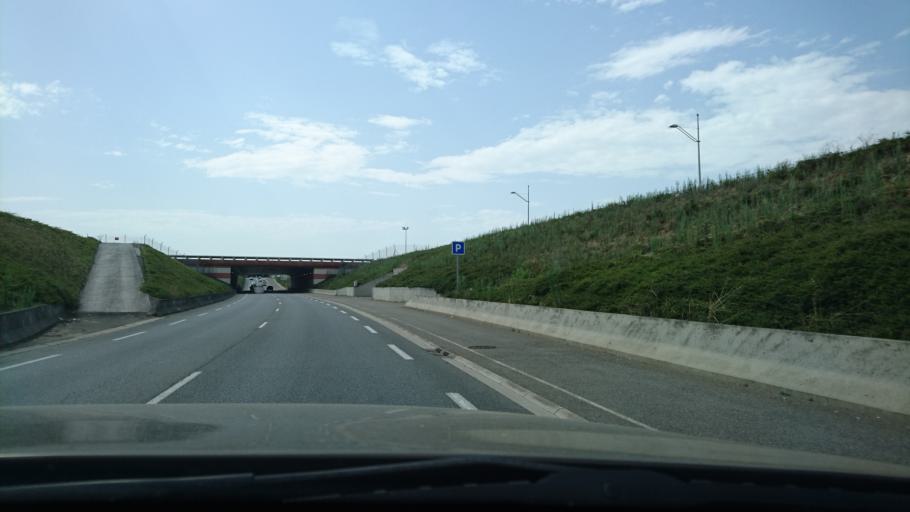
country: FR
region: Midi-Pyrenees
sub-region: Departement de la Haute-Garonne
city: Beauzelle
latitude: 43.6453
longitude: 1.3555
